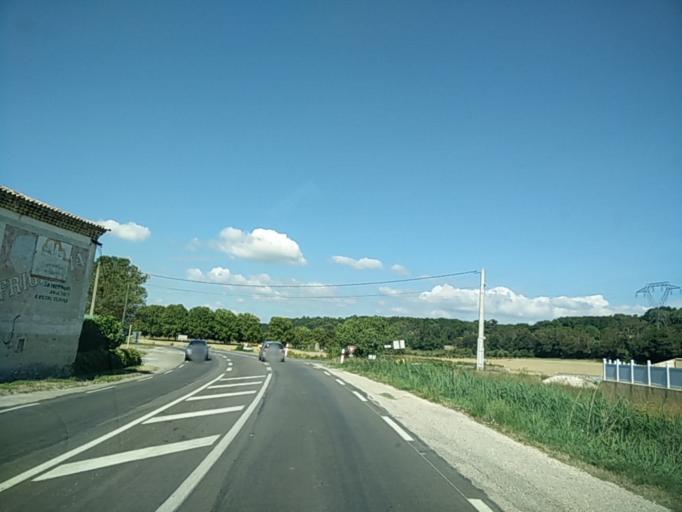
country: FR
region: Rhone-Alpes
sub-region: Departement de la Drome
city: Montboucher-sur-Jabron
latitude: 44.5483
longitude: 4.7994
